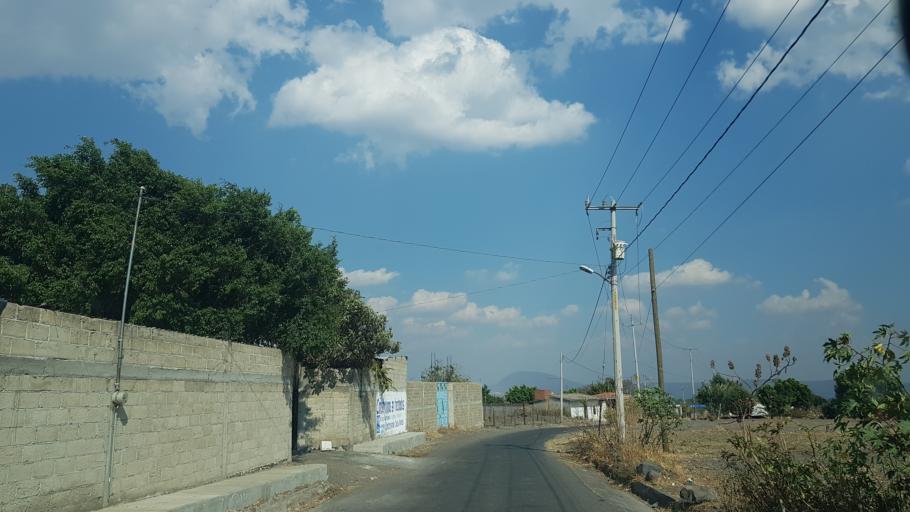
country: MX
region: Puebla
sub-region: Atlixco
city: Colonia Agricola de Ocotepec (Colonia San Jose)
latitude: 18.8938
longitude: -98.5105
